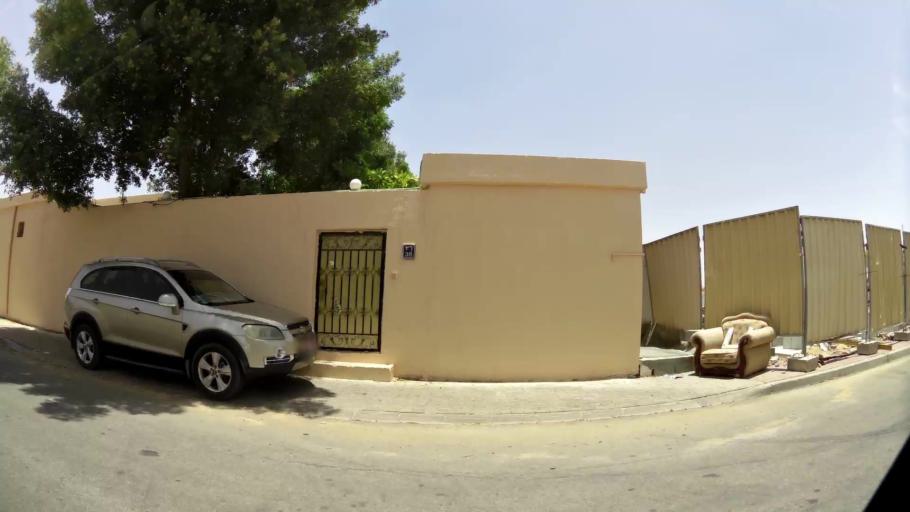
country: OM
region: Al Buraimi
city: Al Buraymi
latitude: 24.2651
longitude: 55.7365
